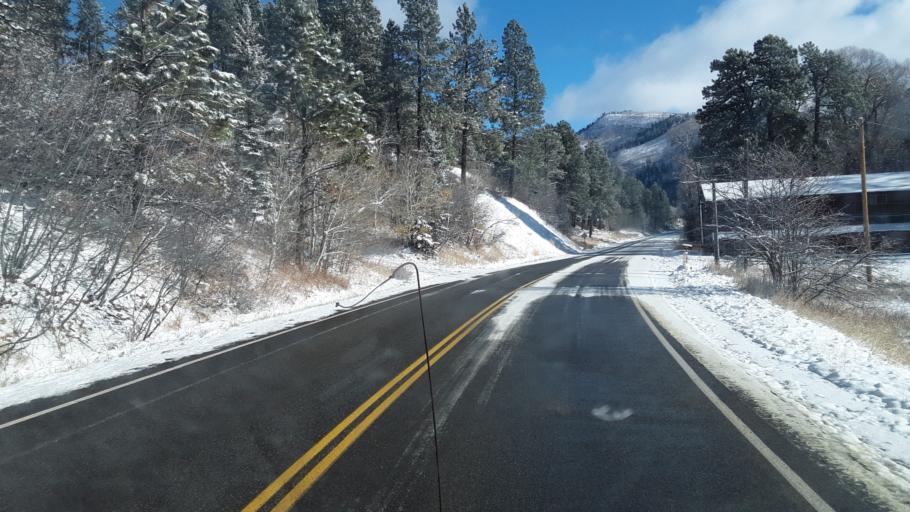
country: US
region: Colorado
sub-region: La Plata County
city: Bayfield
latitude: 37.3571
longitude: -107.6789
